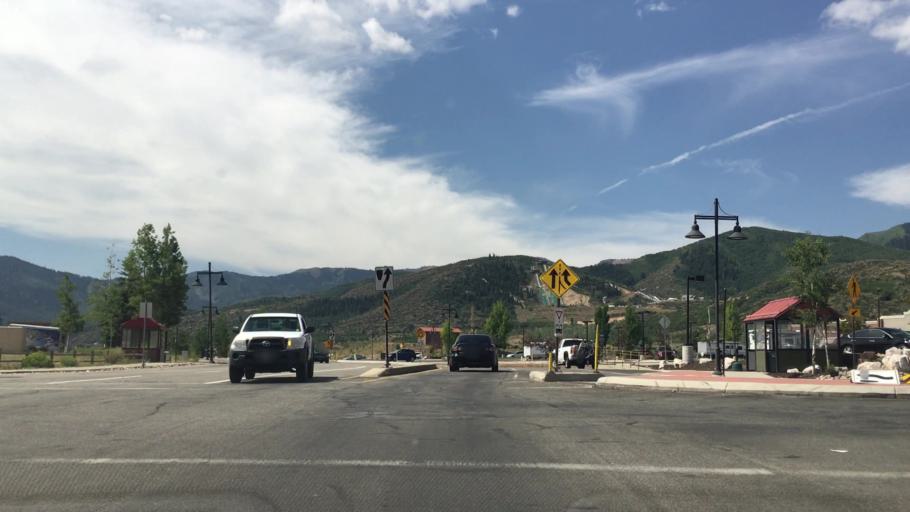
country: US
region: Utah
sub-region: Summit County
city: Snyderville
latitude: 40.7259
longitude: -111.5471
